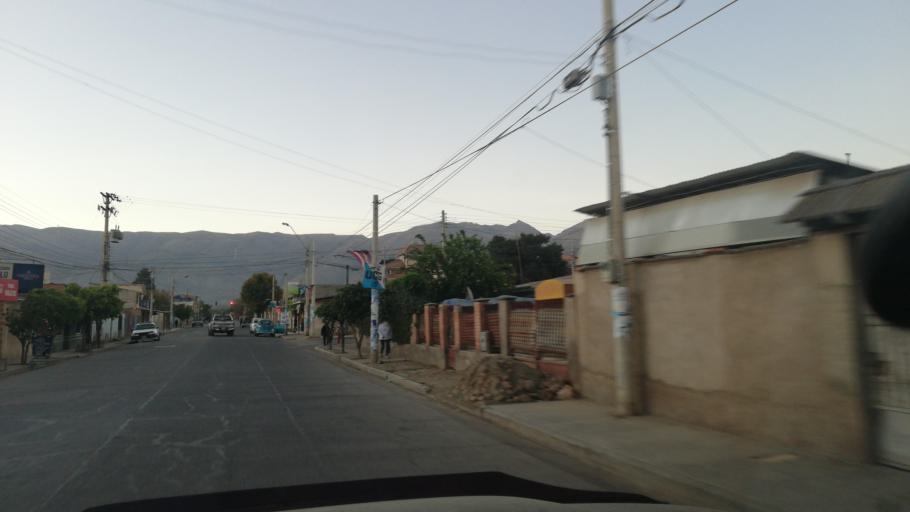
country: BO
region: Cochabamba
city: Cochabamba
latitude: -17.3904
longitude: -66.2193
